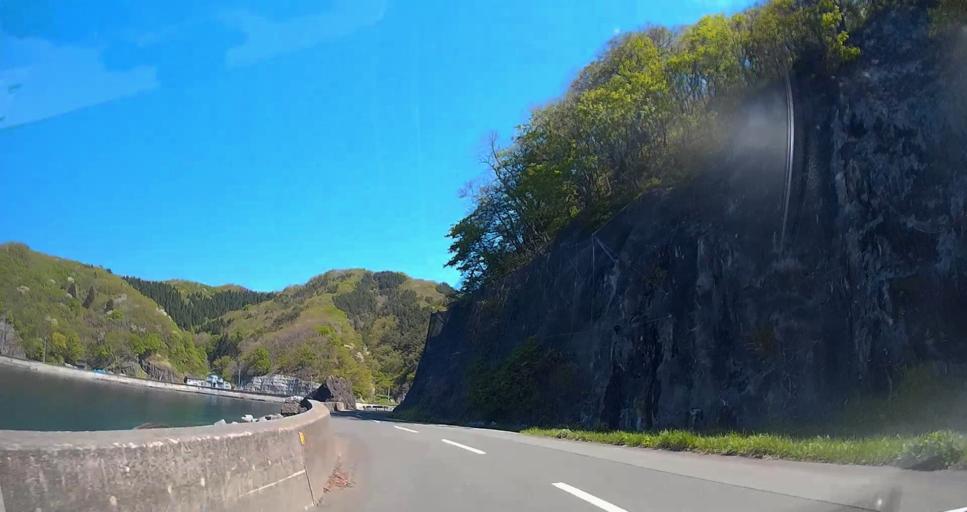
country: JP
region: Aomori
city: Aomori Shi
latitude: 41.1362
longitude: 140.7780
